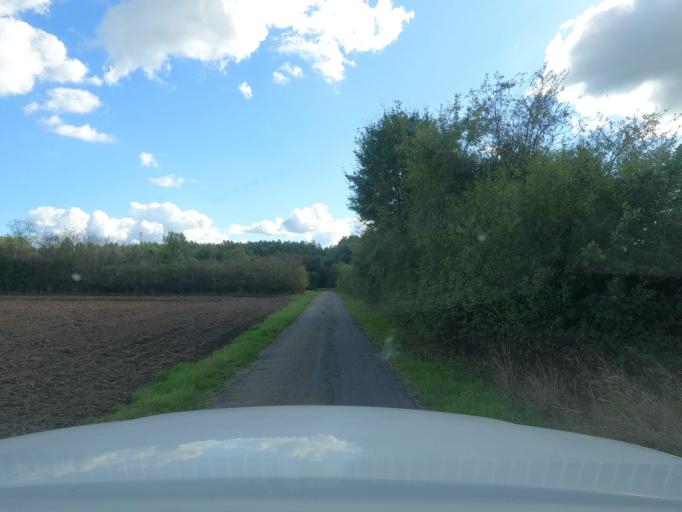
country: DE
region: North Rhine-Westphalia
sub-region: Regierungsbezirk Dusseldorf
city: Hunxe
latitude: 51.6591
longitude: 6.7983
